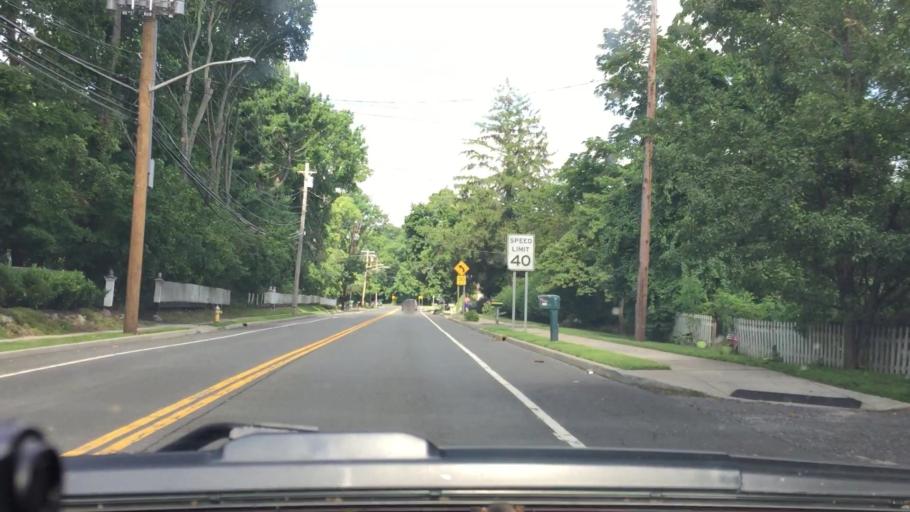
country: US
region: New York
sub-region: Suffolk County
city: East Setauket
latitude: 40.9437
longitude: -73.0977
